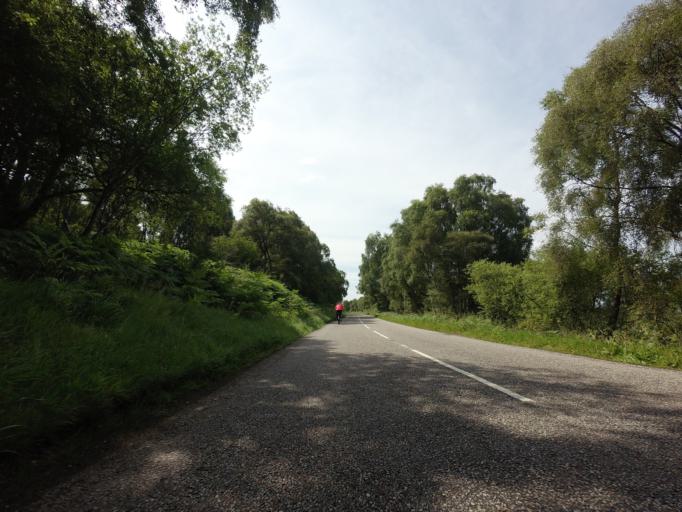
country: GB
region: Scotland
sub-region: Highland
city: Alness
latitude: 57.8574
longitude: -4.2434
